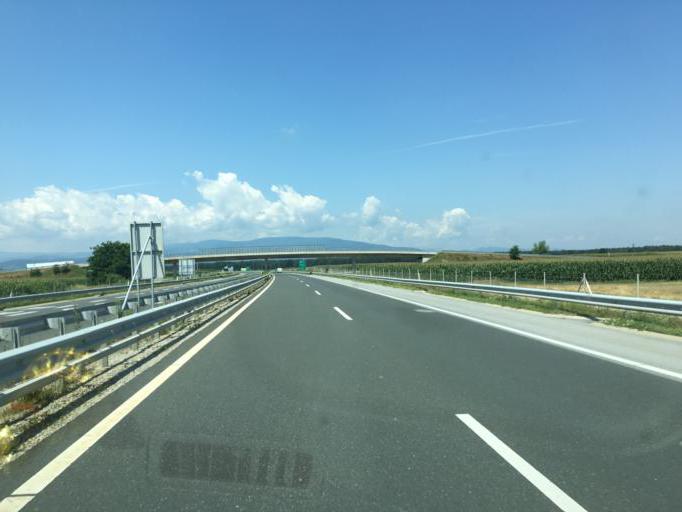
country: SI
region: Starse
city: Starse
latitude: 46.4552
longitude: 15.7517
